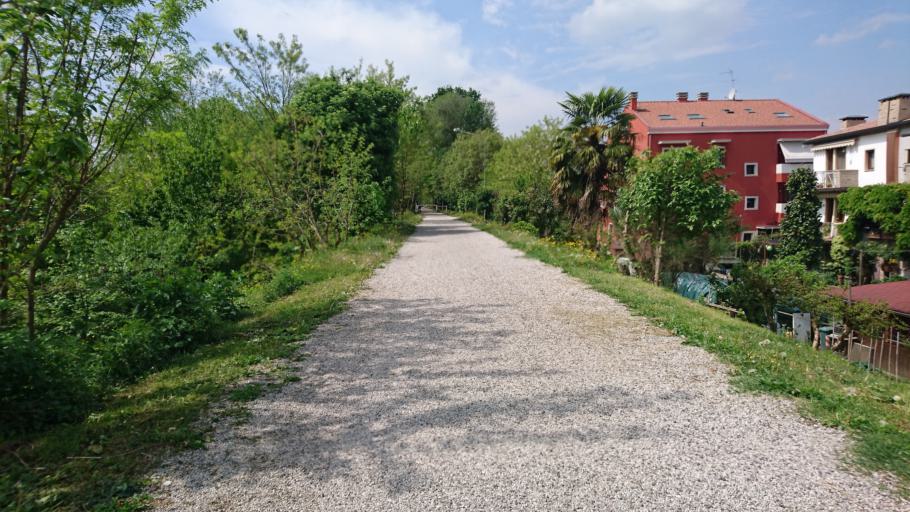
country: IT
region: Veneto
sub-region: Provincia di Padova
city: Vigodarzere
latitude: 45.4547
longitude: 11.8779
